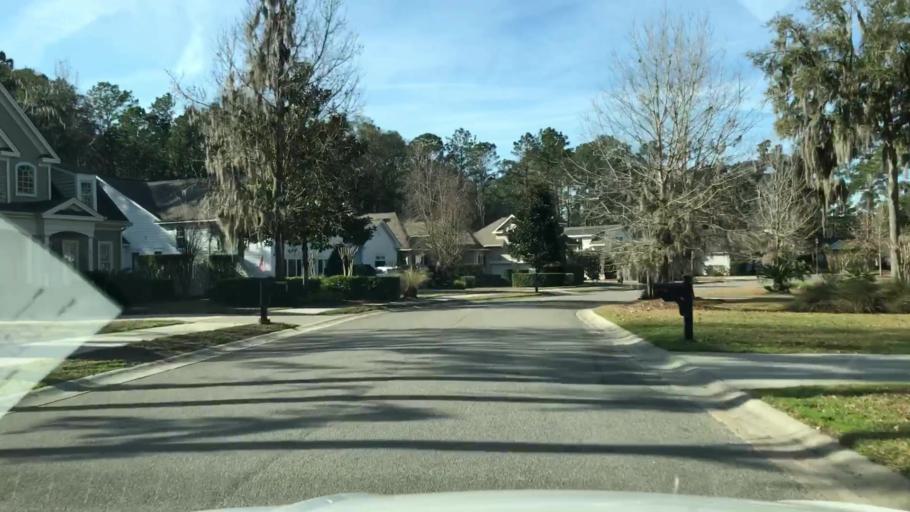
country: US
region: South Carolina
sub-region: Beaufort County
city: Bluffton
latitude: 32.2392
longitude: -80.9152
